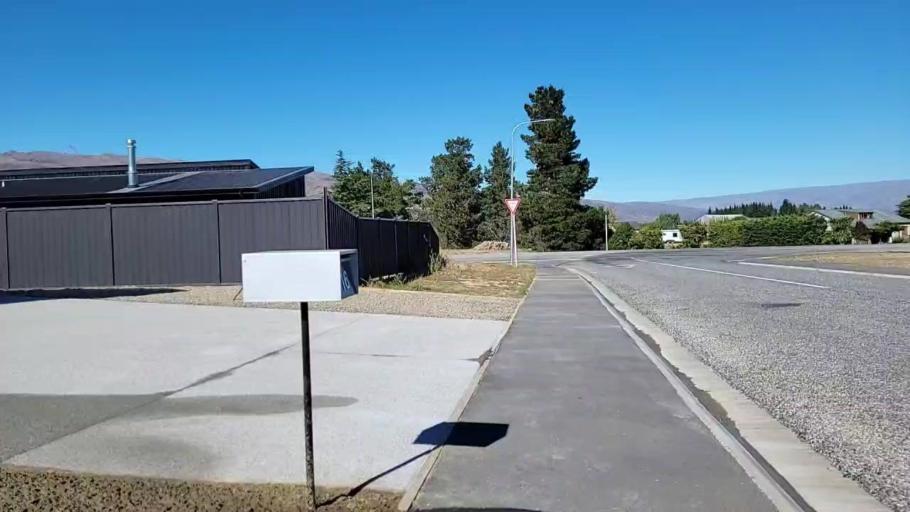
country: NZ
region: Otago
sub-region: Queenstown-Lakes District
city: Wanaka
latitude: -44.9771
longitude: 169.2375
